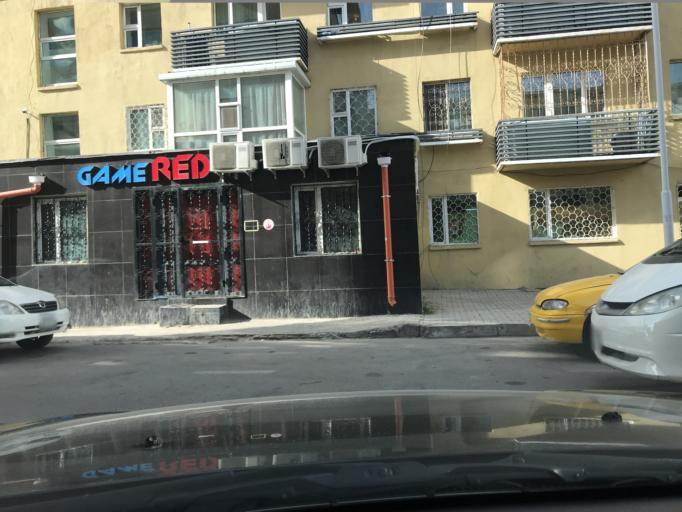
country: MN
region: Ulaanbaatar
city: Ulaanbaatar
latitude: 47.9176
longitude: 106.9054
